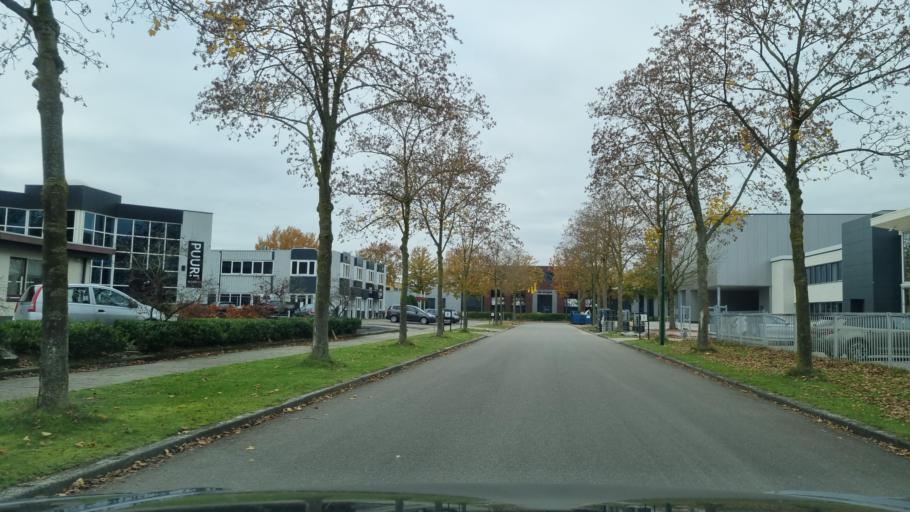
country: NL
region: Utrecht
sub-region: Gemeente Veenendaal
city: Veenendaal
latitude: 52.0402
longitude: 5.5469
